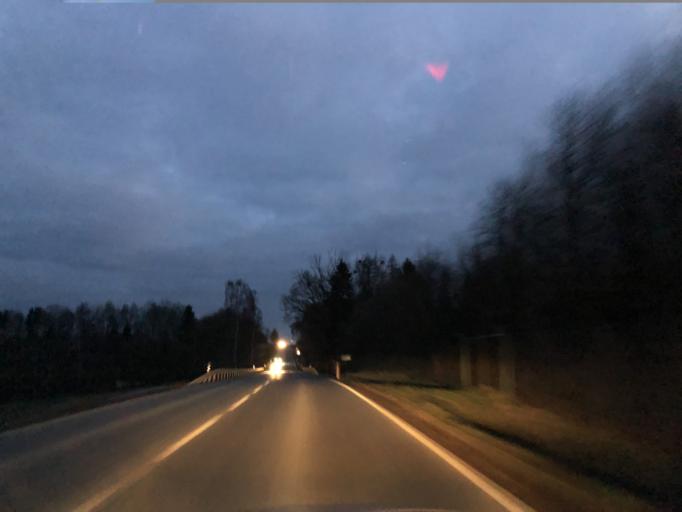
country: DE
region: Rheinland-Pfalz
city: Singhofen
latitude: 50.2904
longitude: 7.8229
